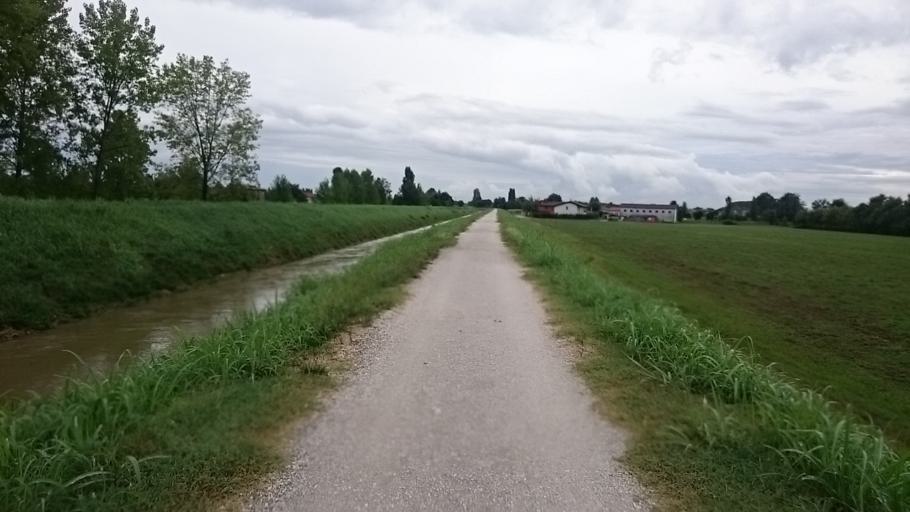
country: IT
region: Veneto
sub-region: Provincia di Padova
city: Loreggiola
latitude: 45.6095
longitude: 11.9302
